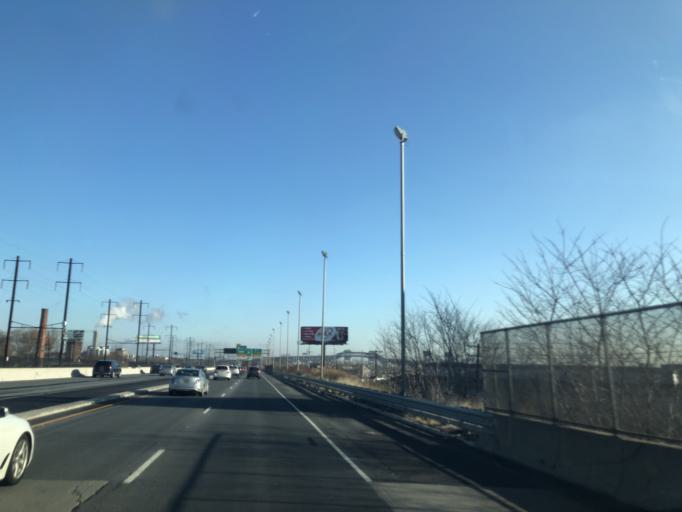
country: US
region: New Jersey
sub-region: Hudson County
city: Harrison
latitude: 40.7262
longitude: -74.1355
